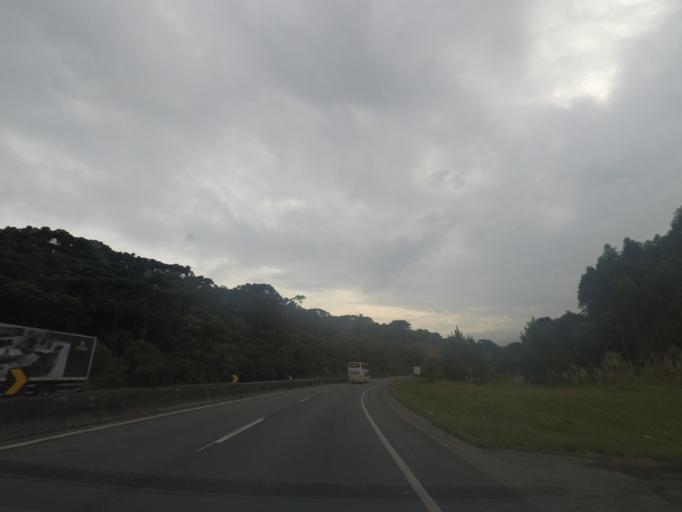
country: BR
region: Parana
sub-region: Campina Grande Do Sul
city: Campina Grande do Sul
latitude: -25.3106
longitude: -49.0027
